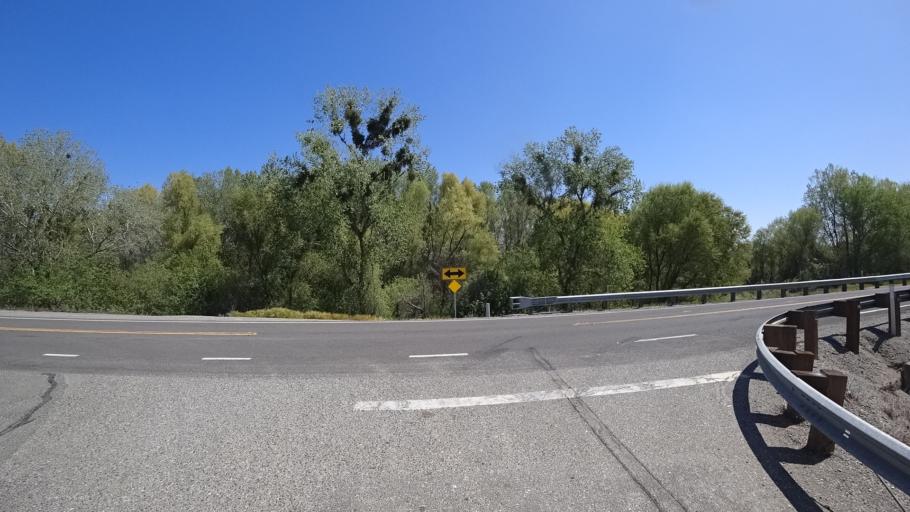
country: US
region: California
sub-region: Glenn County
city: Hamilton City
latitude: 39.5581
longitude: -122.0045
